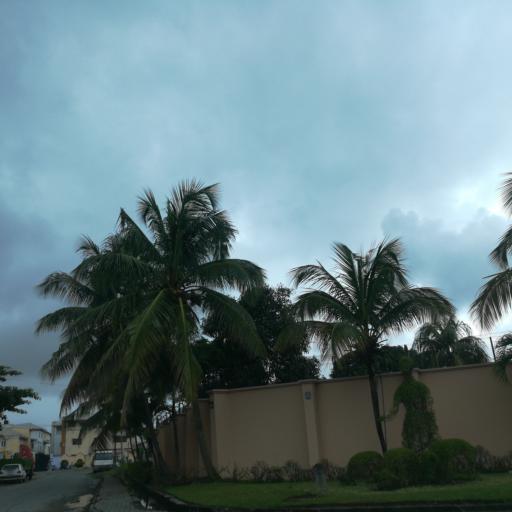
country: NG
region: Lagos
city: Ikoyi
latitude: 6.4397
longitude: 3.4614
